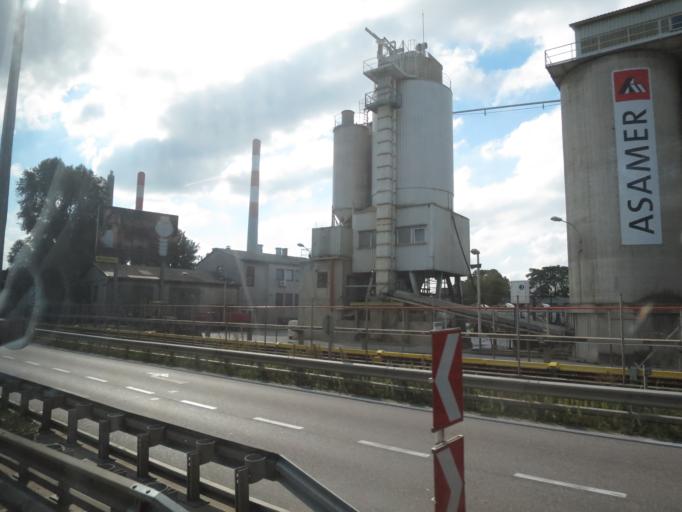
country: AT
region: Vienna
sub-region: Wien Stadt
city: Vienna
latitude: 48.1865
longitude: 16.4290
